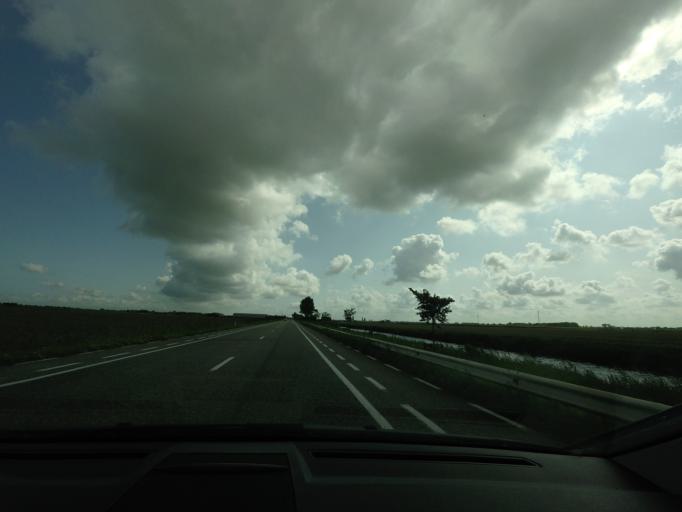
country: BE
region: Flanders
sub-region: Provincie West-Vlaanderen
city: Bredene
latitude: 51.2280
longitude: 3.0175
